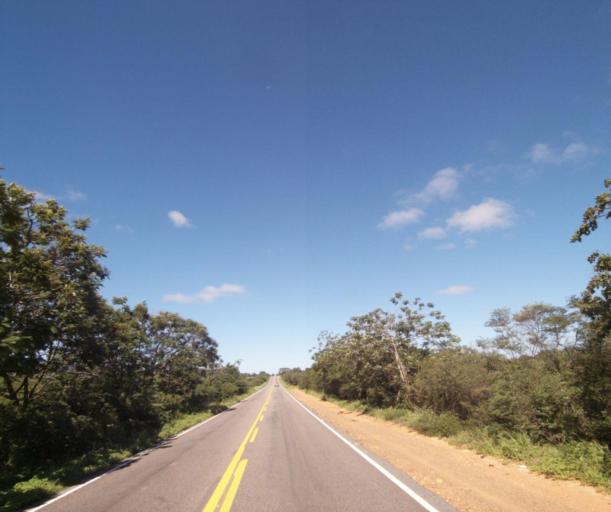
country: BR
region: Bahia
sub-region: Palmas De Monte Alto
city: Palmas de Monte Alto
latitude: -14.2434
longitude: -43.0862
